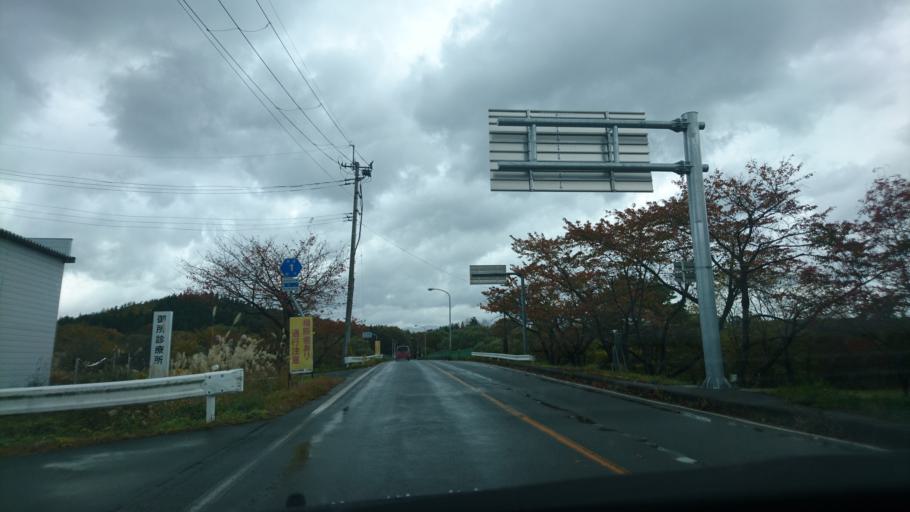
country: JP
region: Iwate
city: Shizukuishi
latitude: 39.6636
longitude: 140.9699
